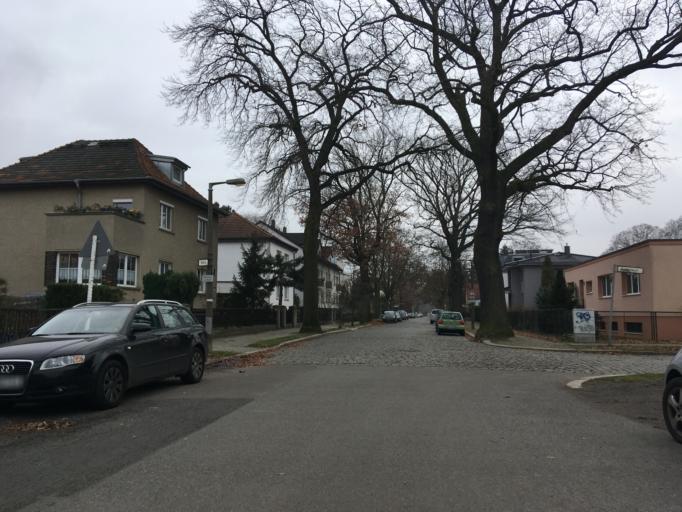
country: DE
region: Berlin
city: Wilhelmsruh
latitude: 52.5846
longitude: 13.3785
